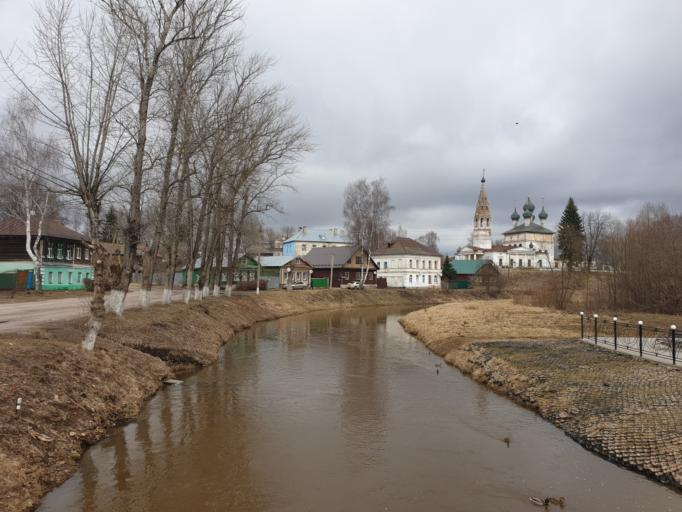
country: RU
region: Kostroma
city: Nerekhta
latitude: 57.4611
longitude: 40.5710
